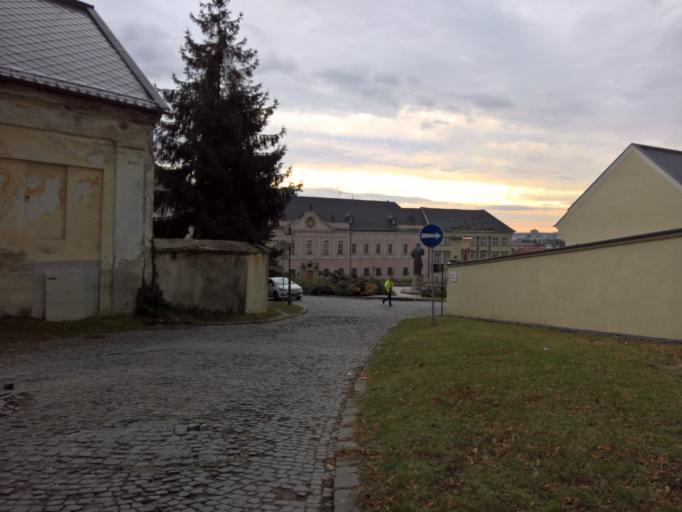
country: SK
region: Nitriansky
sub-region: Okres Nitra
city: Nitra
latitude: 48.3170
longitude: 18.0882
